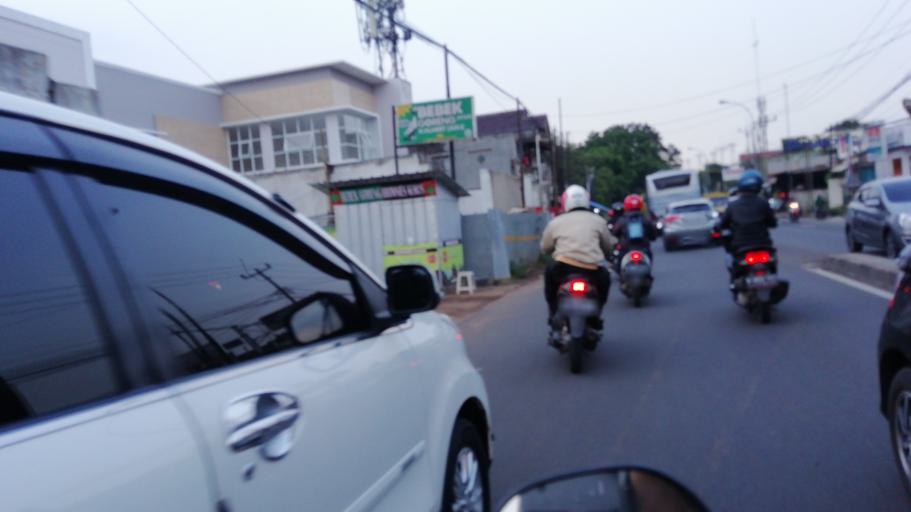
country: ID
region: West Java
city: Depok
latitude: -6.4042
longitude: 106.8617
